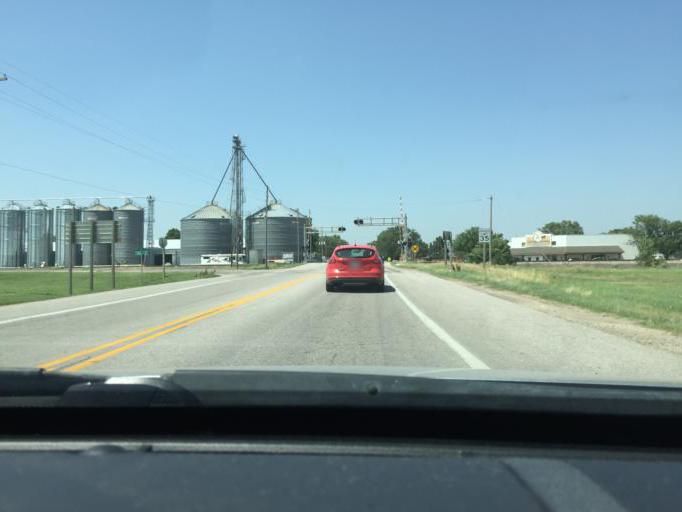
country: US
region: Kansas
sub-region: Reno County
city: Haven
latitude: 37.9375
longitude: -97.8667
